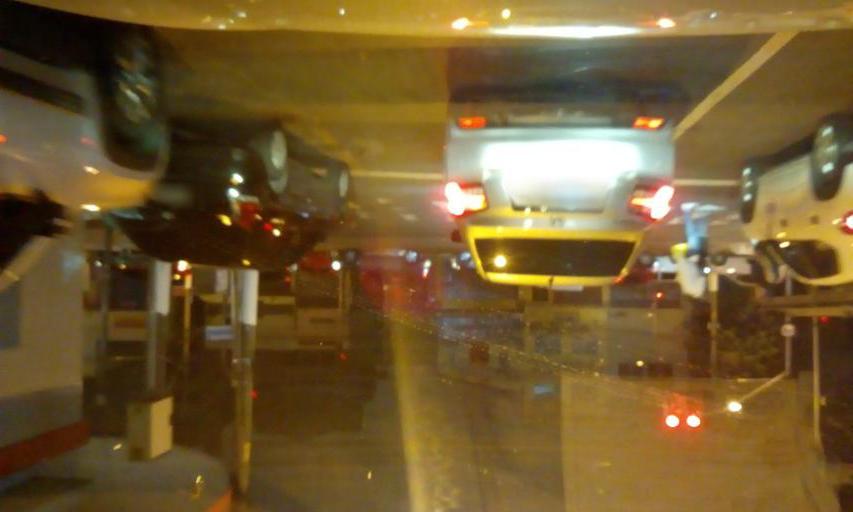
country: BR
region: Sao Paulo
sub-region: Sao Paulo
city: Sao Paulo
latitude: -23.5467
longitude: -46.6226
